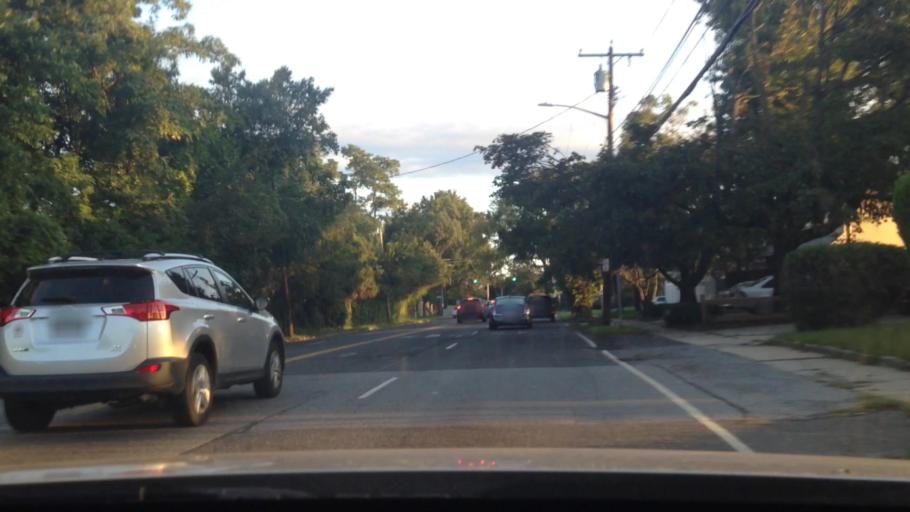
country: US
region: New York
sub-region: Nassau County
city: Lakeview
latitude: 40.6832
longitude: -73.6631
